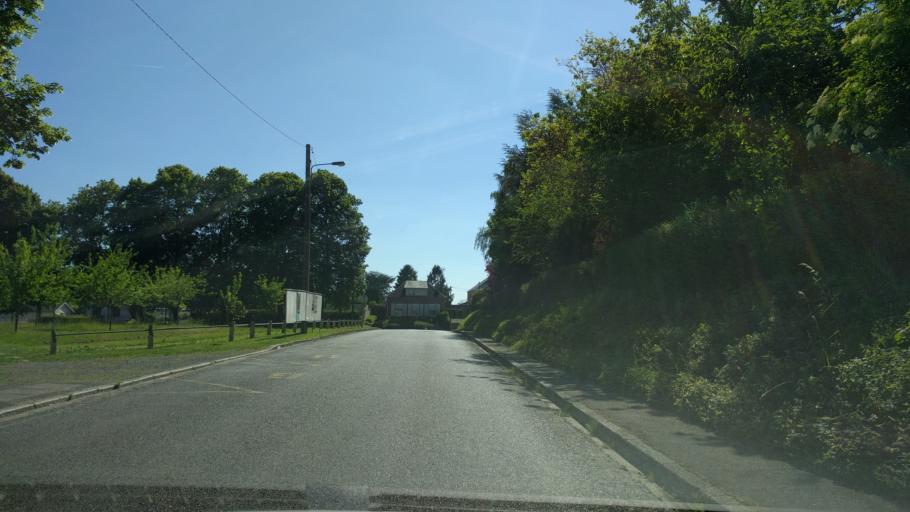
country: FR
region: Picardie
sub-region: Departement de la Somme
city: Peronne
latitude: 49.9286
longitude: 2.9256
